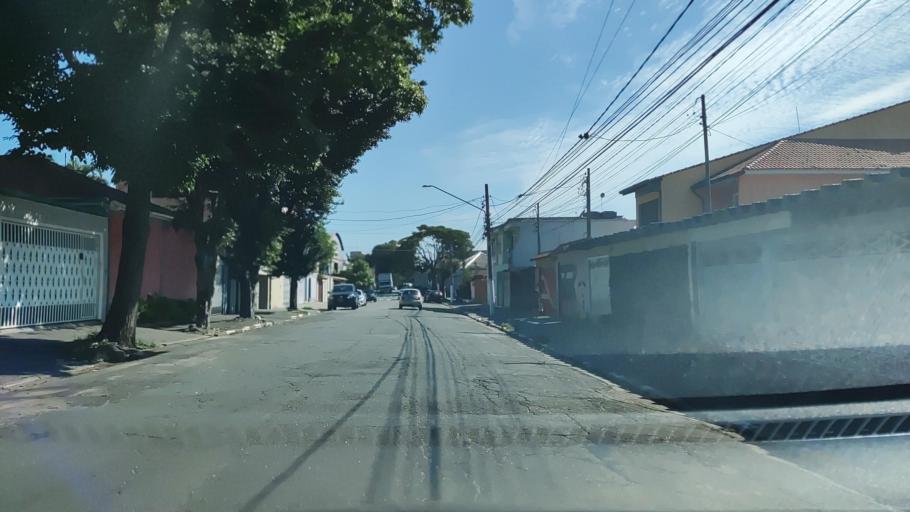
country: BR
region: Sao Paulo
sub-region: Osasco
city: Osasco
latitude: -23.5287
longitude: -46.7657
